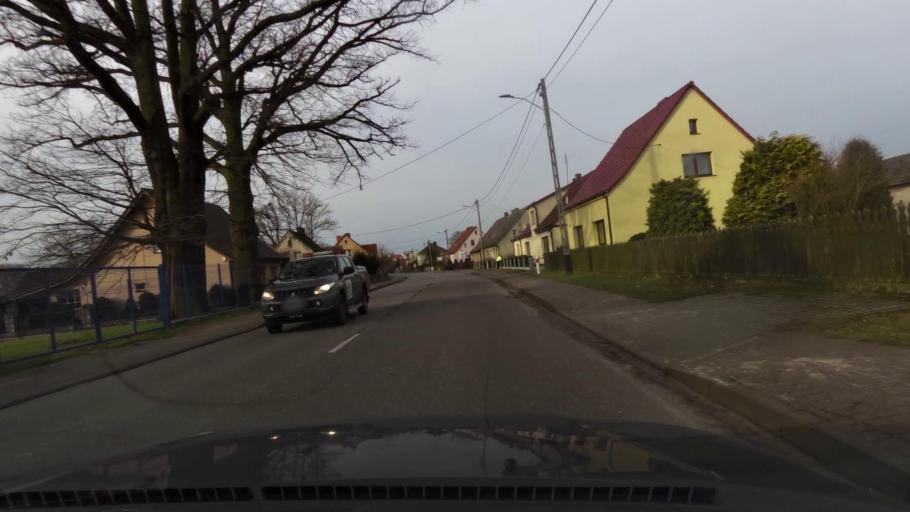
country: PL
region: West Pomeranian Voivodeship
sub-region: Powiat goleniowski
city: Stepnica
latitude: 53.6528
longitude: 14.6357
